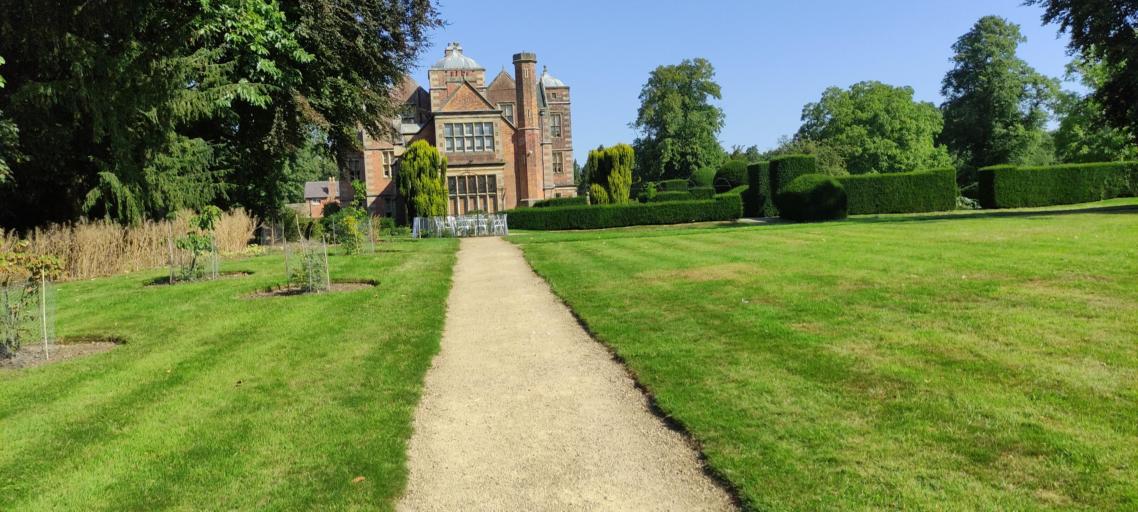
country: GB
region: England
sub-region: North Yorkshire
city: Catterick
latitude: 54.3714
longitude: -1.5789
